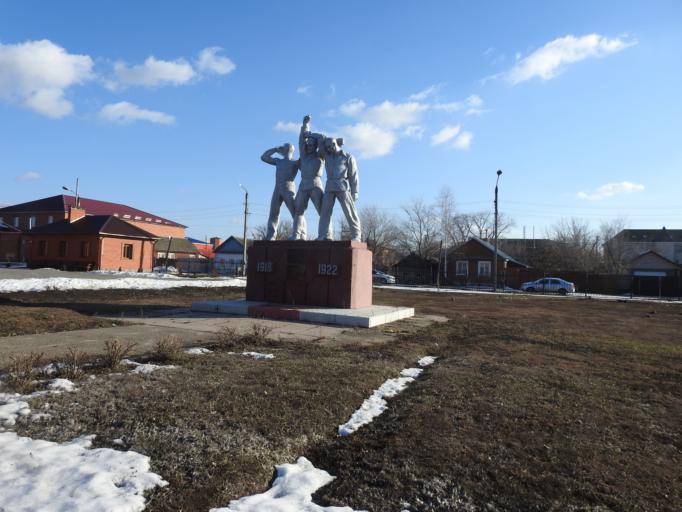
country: RU
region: Saratov
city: Yershov
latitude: 51.3505
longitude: 48.2732
